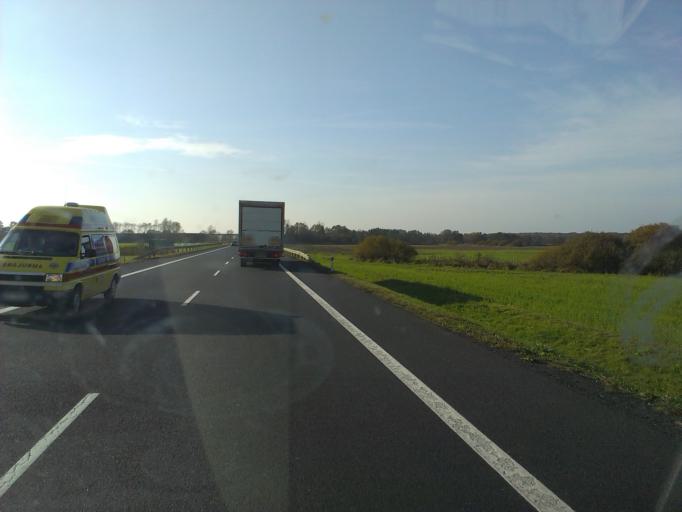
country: PL
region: Lubusz
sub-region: Powiat zielonogorski
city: Sulechow
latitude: 52.0091
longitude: 15.6109
